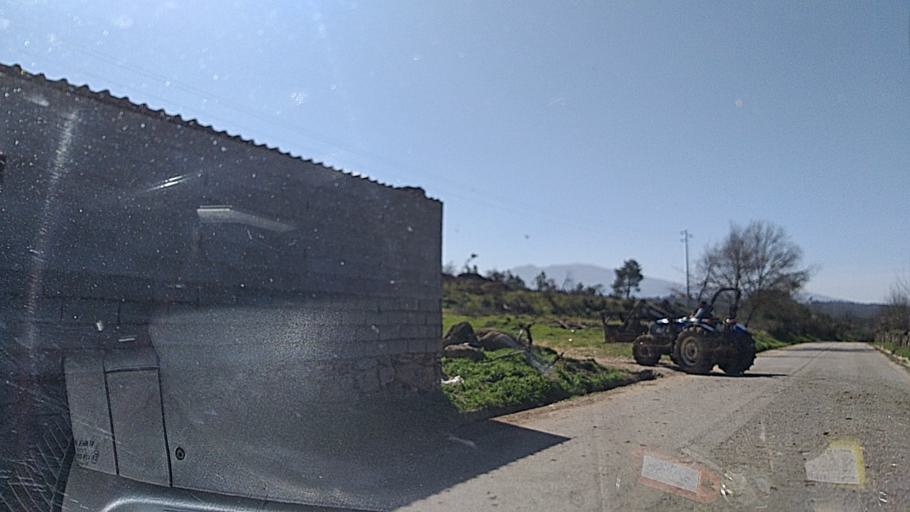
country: PT
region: Guarda
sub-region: Fornos de Algodres
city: Fornos de Algodres
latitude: 40.5926
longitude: -7.4730
